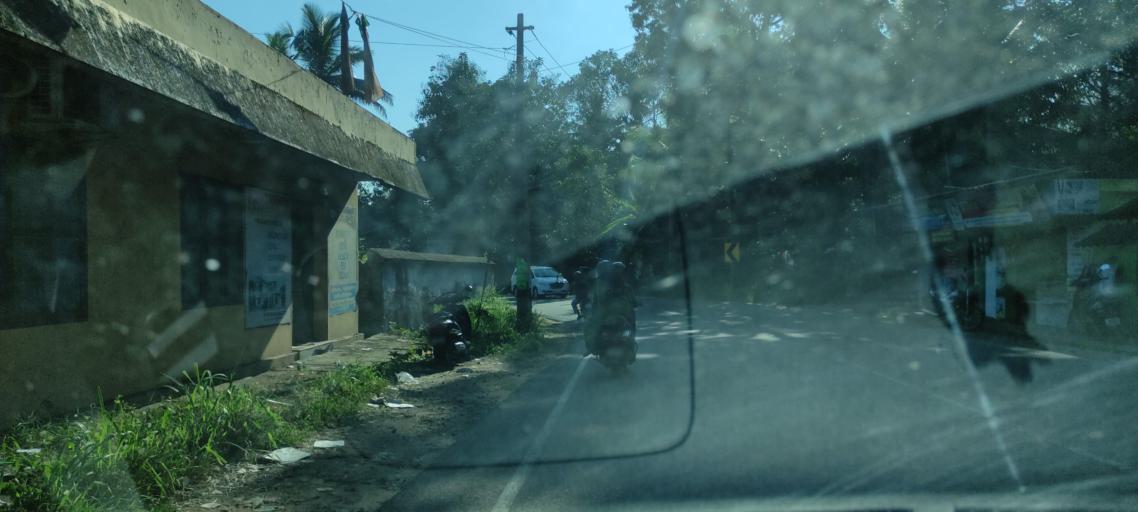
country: IN
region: Kerala
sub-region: Pattanamtitta
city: Pathanamthitta
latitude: 9.2505
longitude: 76.7583
